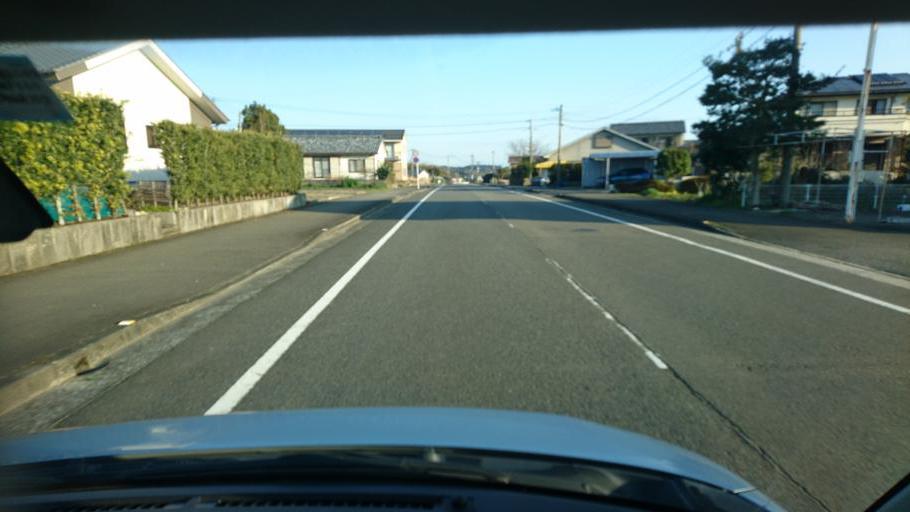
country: JP
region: Miyazaki
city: Miyazaki-shi
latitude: 31.8342
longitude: 131.4198
